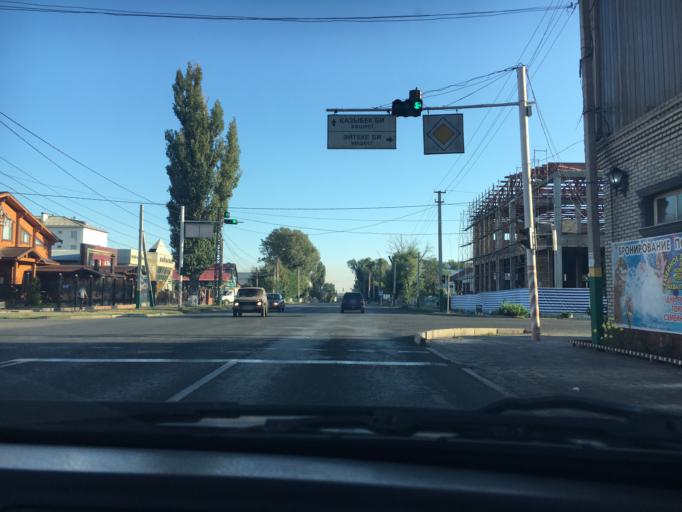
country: KZ
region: Zhambyl
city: Taraz
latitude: 42.8947
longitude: 71.3605
